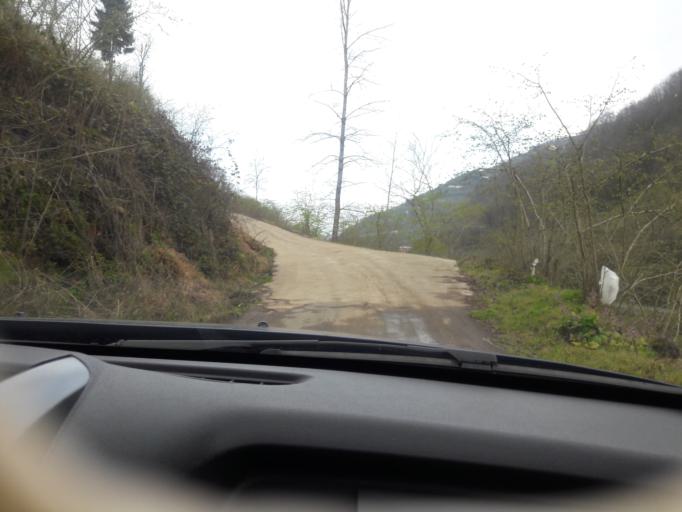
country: TR
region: Trabzon
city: Salpazari
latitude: 40.9702
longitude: 39.1973
